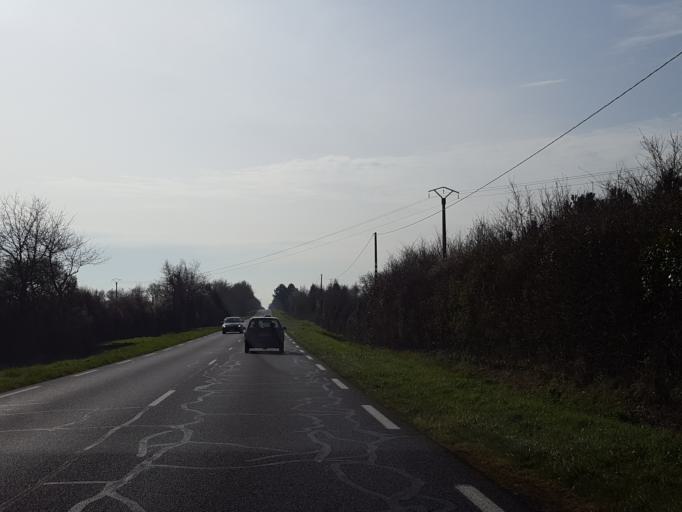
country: FR
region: Pays de la Loire
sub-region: Departement de la Vendee
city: Saligny
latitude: 46.8135
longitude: -1.4627
